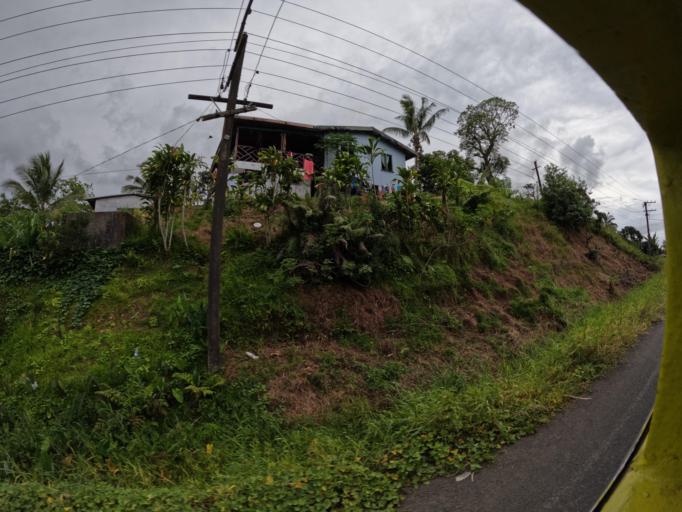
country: FJ
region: Central
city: Suva
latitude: -18.0779
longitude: 178.4589
